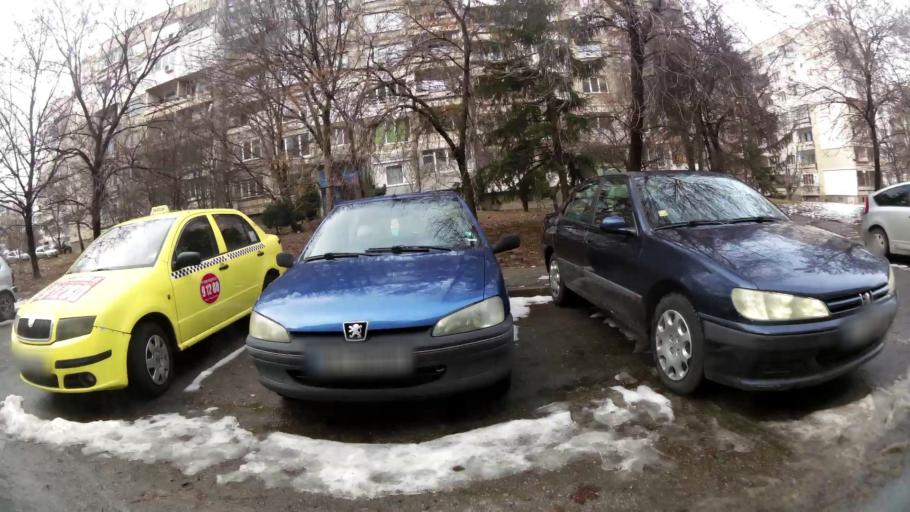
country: BG
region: Sofiya
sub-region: Obshtina Bozhurishte
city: Bozhurishte
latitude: 42.7149
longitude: 23.2477
